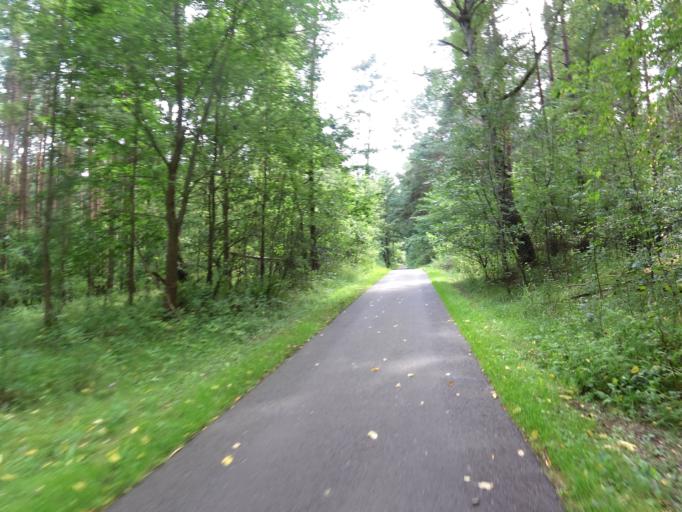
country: DE
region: Brandenburg
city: Lychen
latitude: 53.2410
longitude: 13.2928
